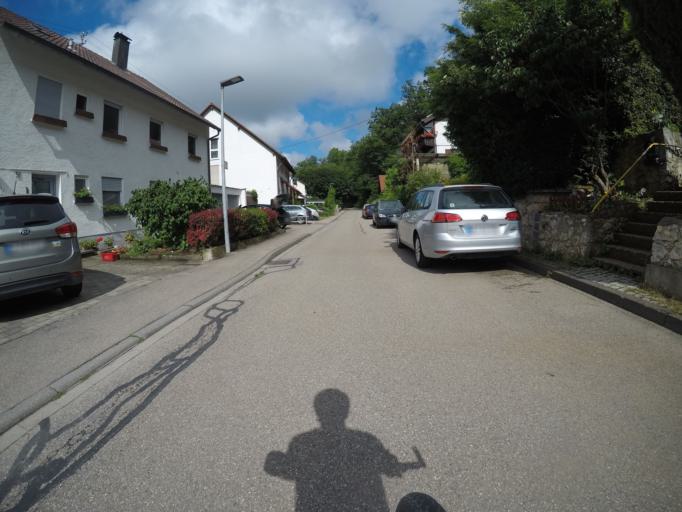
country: DE
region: Baden-Wuerttemberg
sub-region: Tuebingen Region
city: Westerstetten
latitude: 48.5229
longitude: 9.9515
